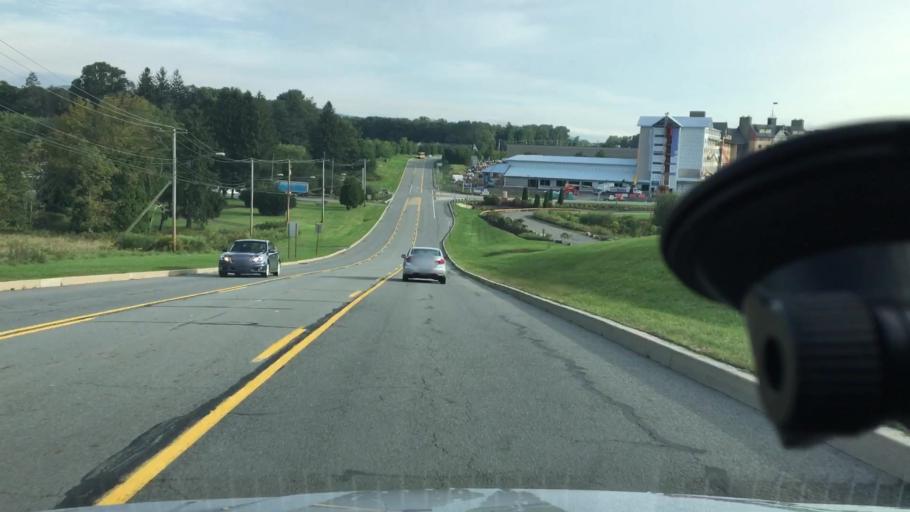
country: US
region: Pennsylvania
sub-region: Monroe County
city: Mount Pocono
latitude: 41.1100
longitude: -75.3248
